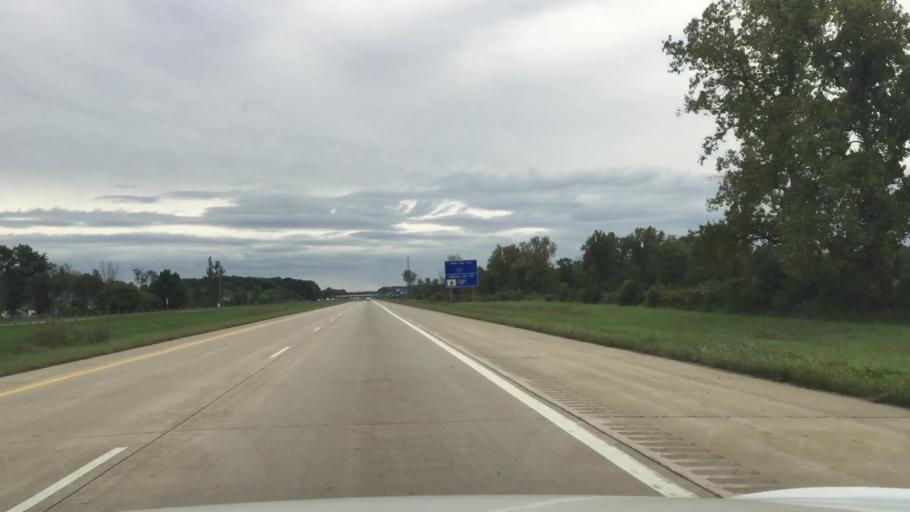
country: US
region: Michigan
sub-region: Saint Clair County
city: Marysville
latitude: 42.9334
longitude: -82.5068
